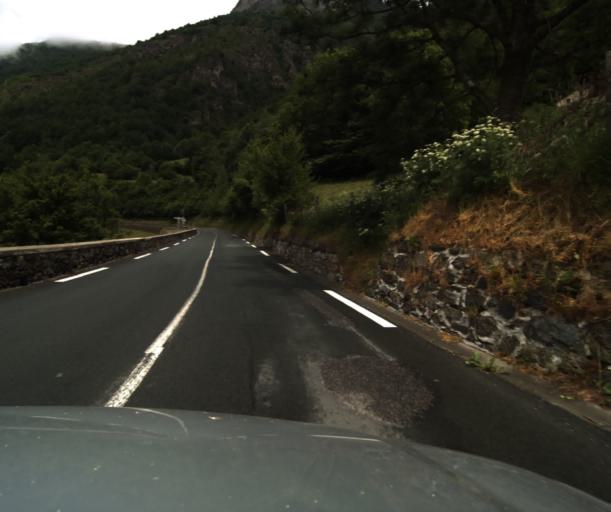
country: FR
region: Midi-Pyrenees
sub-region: Departement des Hautes-Pyrenees
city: Luz-Saint-Sauveur
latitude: 42.7919
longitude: 0.0186
